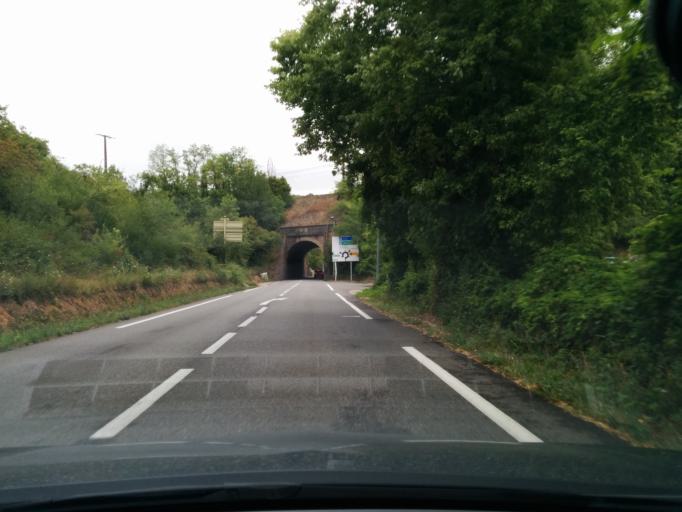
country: FR
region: Midi-Pyrenees
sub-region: Departement du Lot
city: Cahors
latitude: 44.4143
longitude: 1.4334
